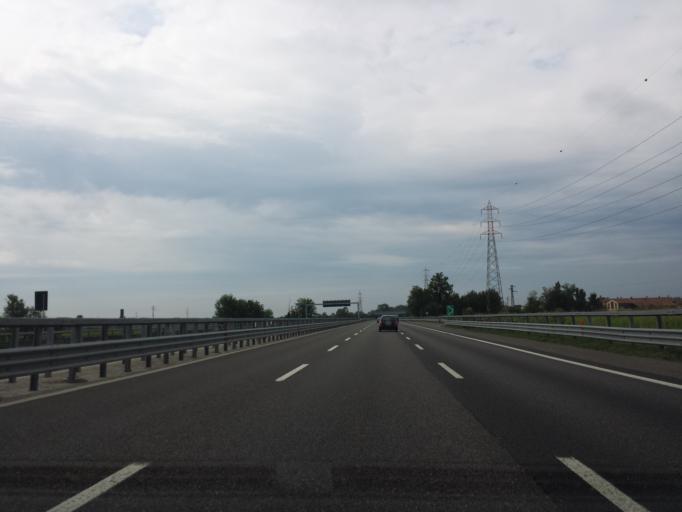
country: IT
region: Lombardy
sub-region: Citta metropolitana di Milano
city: Rozzano
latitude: 45.3806
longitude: 9.1335
